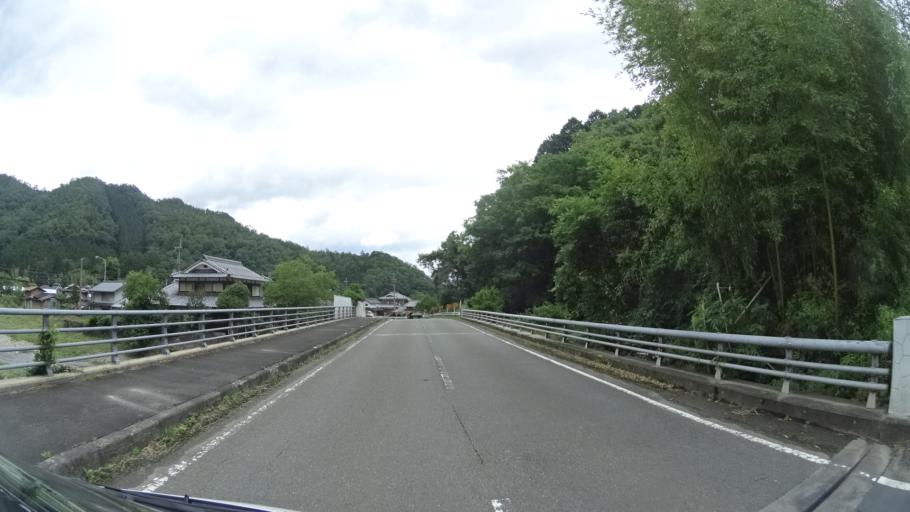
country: JP
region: Kyoto
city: Kameoka
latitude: 35.0938
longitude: 135.4267
